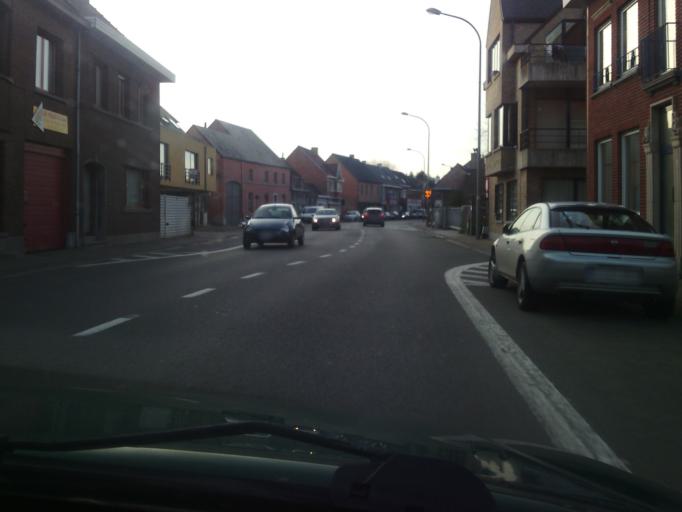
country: BE
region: Flanders
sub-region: Provincie Oost-Vlaanderen
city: Berlare
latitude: 51.0470
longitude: 3.9552
